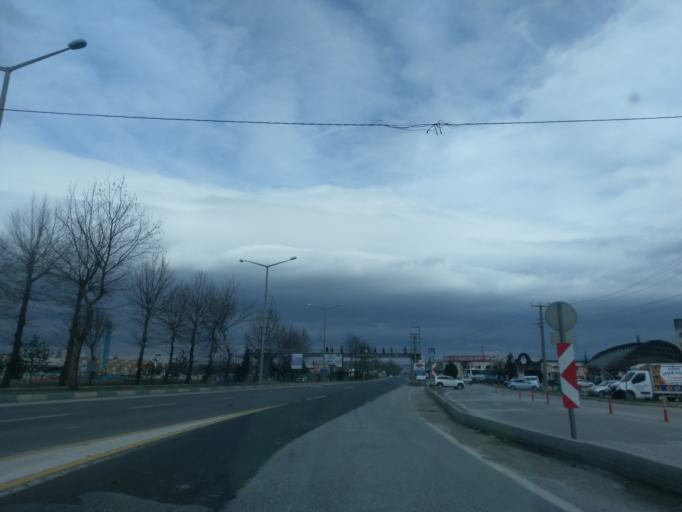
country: TR
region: Kuetahya
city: Kutahya
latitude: 39.4327
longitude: 29.9965
